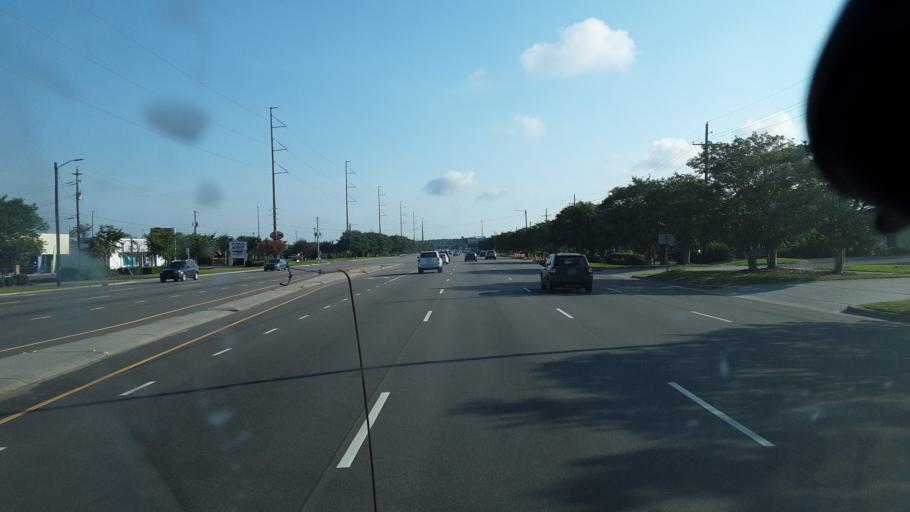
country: US
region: North Carolina
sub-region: New Hanover County
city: Kings Grant
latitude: 34.2315
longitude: -77.8763
